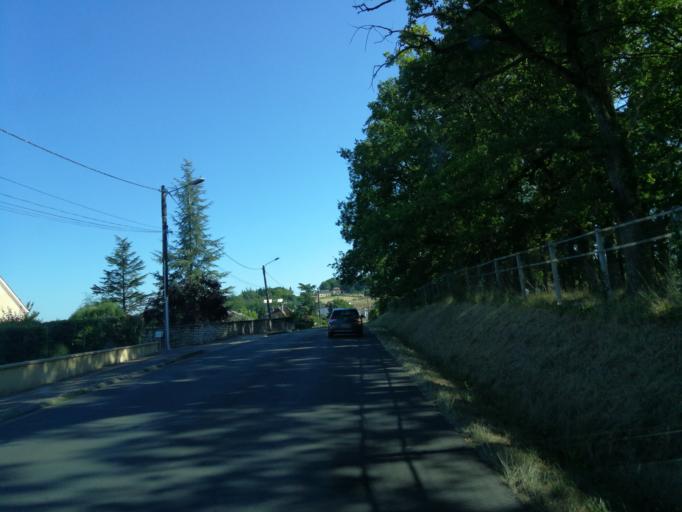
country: FR
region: Midi-Pyrenees
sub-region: Departement du Lot
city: Gourdon
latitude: 44.7294
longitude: 1.3738
